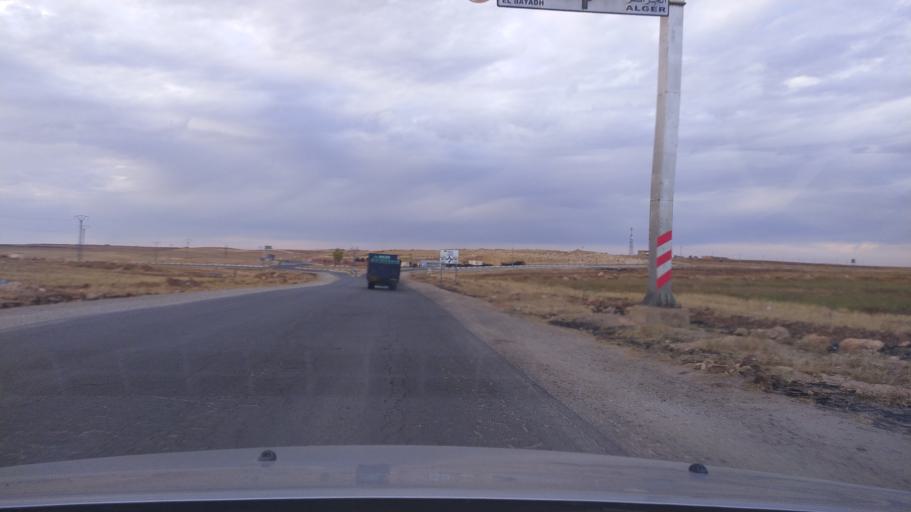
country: DZ
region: Tiaret
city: Frenda
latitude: 34.9901
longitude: 1.1309
